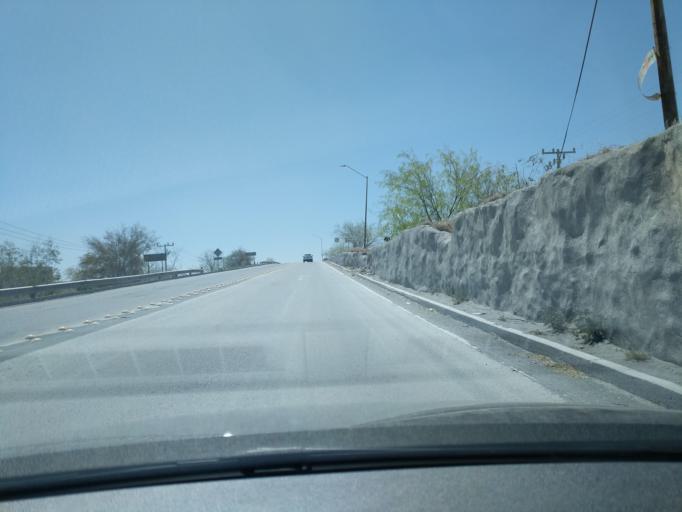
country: MX
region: Nuevo Leon
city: Apodaca
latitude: 25.7964
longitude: -100.1571
